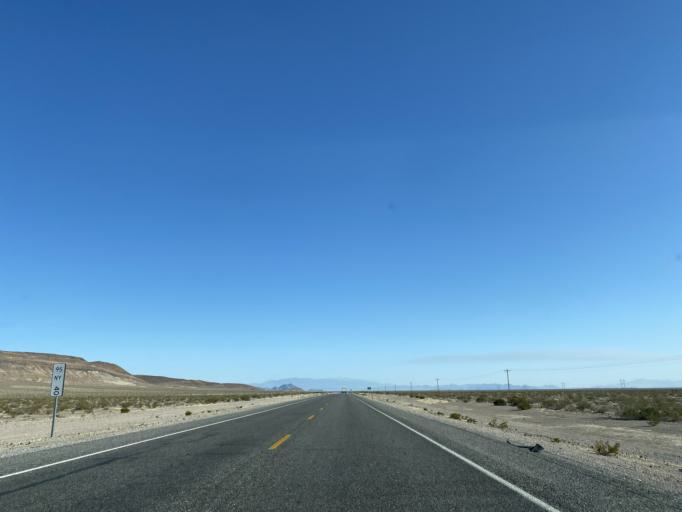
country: US
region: Nevada
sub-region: Nye County
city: Beatty
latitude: 36.6908
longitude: -116.5637
